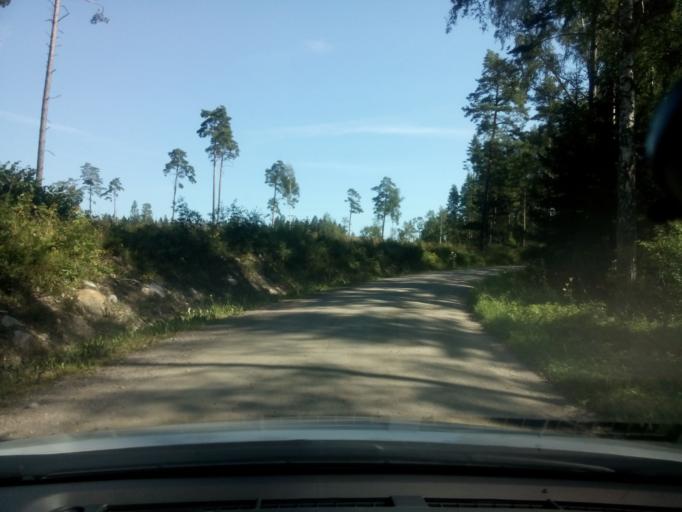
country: SE
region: Soedermanland
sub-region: Oxelosunds Kommun
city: Oxelosund
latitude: 58.7381
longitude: 17.1469
